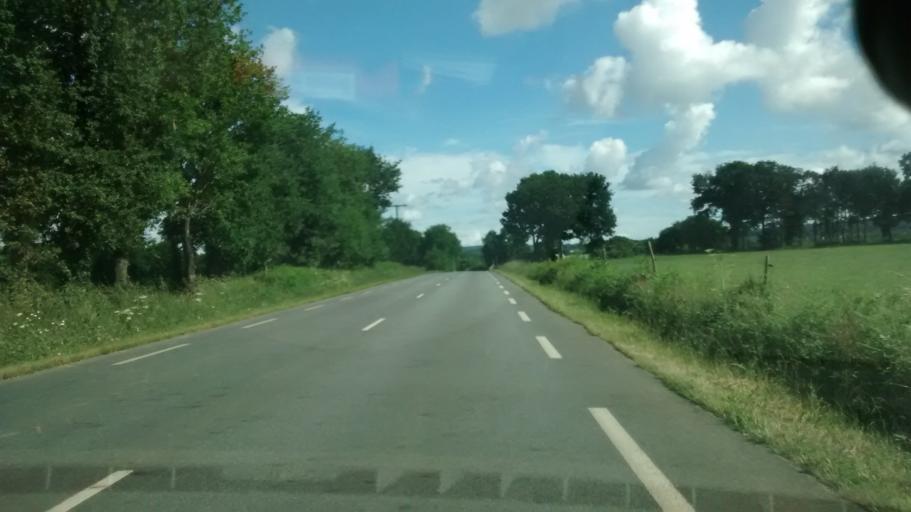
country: FR
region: Brittany
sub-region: Departement du Morbihan
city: Malestroit
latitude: 47.8455
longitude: -2.4165
